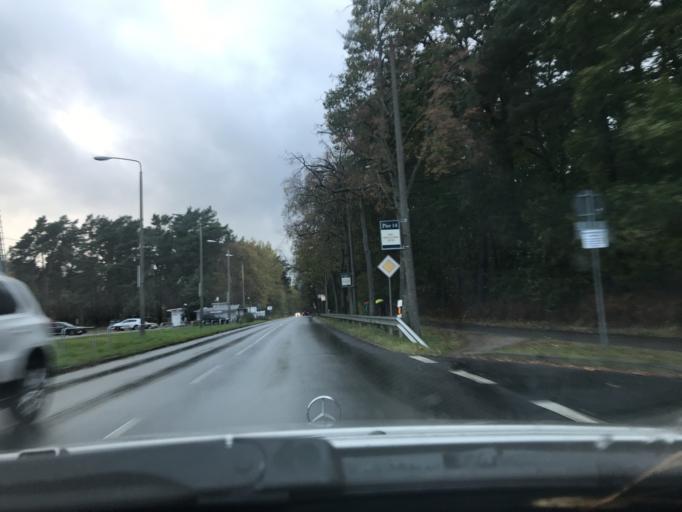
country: PL
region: West Pomeranian Voivodeship
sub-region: Swinoujscie
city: Swinoujscie
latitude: 53.9235
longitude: 14.2144
